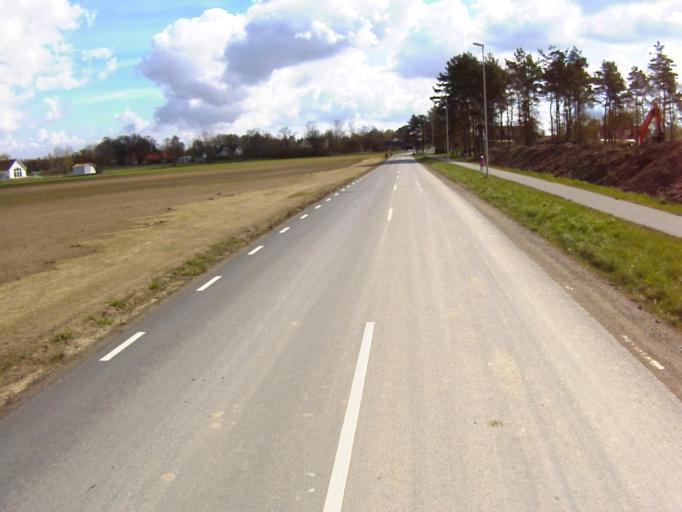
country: SE
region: Skane
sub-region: Kristianstads Kommun
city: Norra Asum
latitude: 56.0099
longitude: 14.0857
